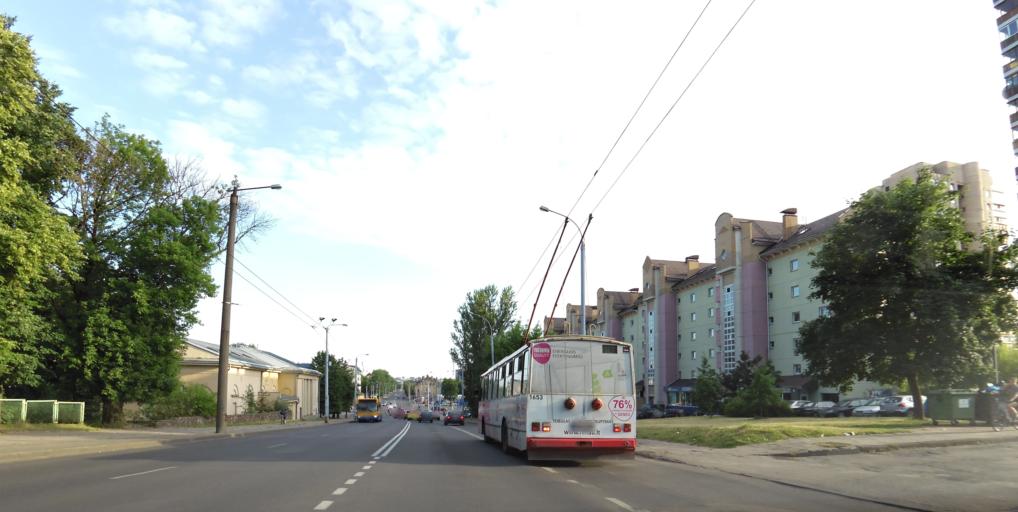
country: LT
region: Vilnius County
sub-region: Vilnius
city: Vilnius
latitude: 54.7056
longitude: 25.2842
